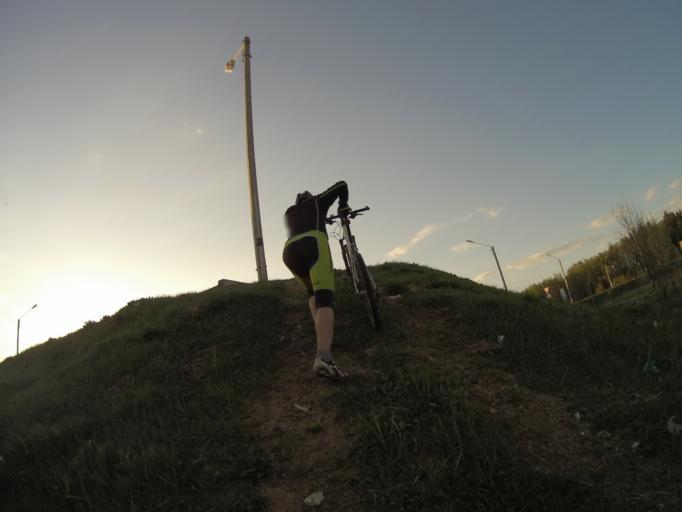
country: RU
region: Vladimir
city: Orgtrud
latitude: 56.1025
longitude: 40.6853
